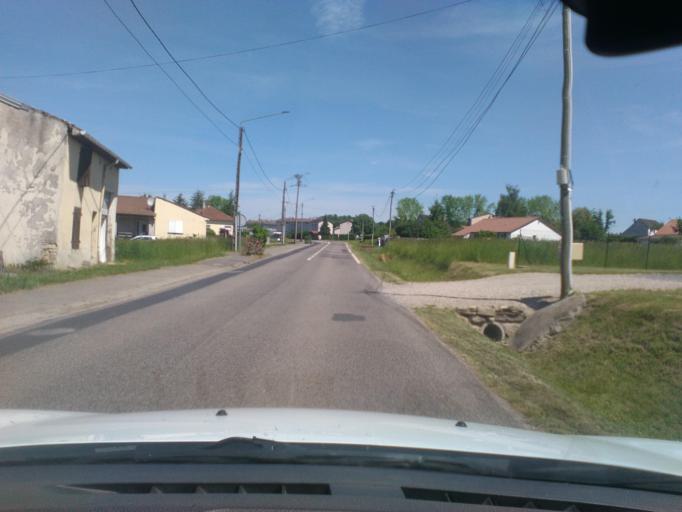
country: FR
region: Lorraine
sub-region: Departement de Meurthe-et-Moselle
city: Gerbeviller
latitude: 48.4477
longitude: 6.5638
